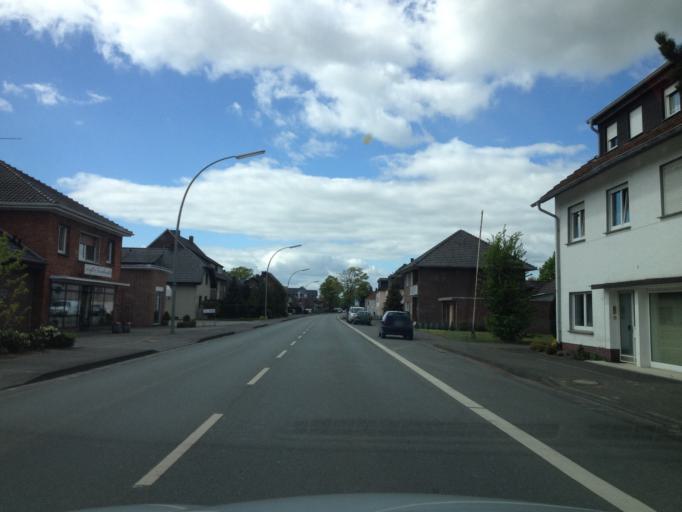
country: DE
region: North Rhine-Westphalia
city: Rietberg
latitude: 51.8153
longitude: 8.4918
